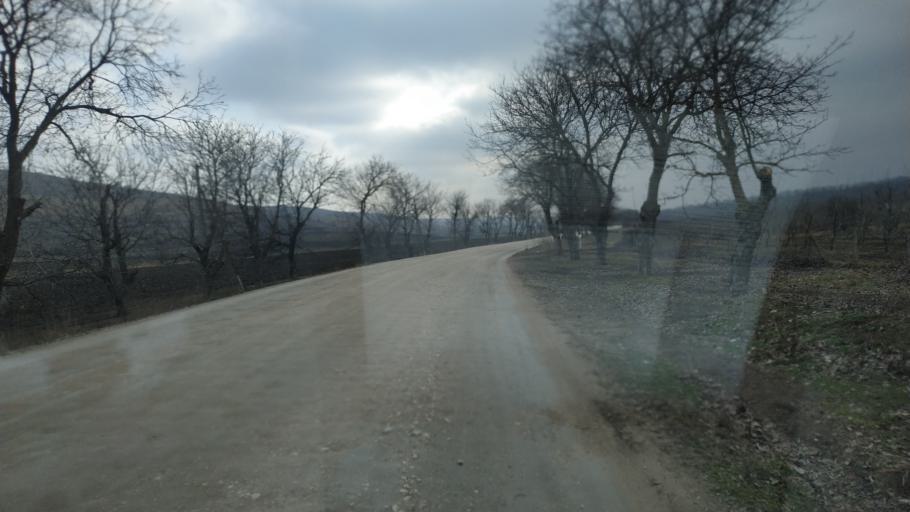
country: MD
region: Hincesti
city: Dancu
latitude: 46.9122
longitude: 28.3292
